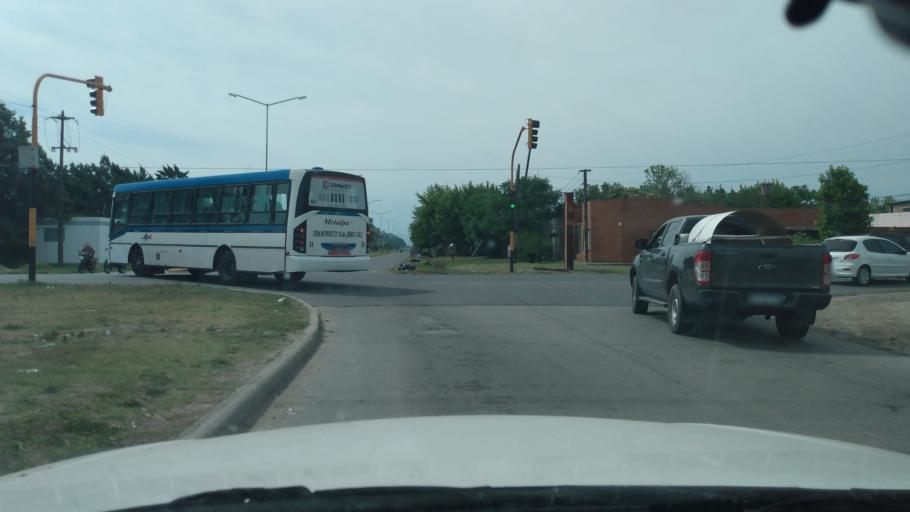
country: AR
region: Buenos Aires
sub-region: Partido de Lujan
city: Lujan
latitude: -34.5582
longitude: -59.1295
